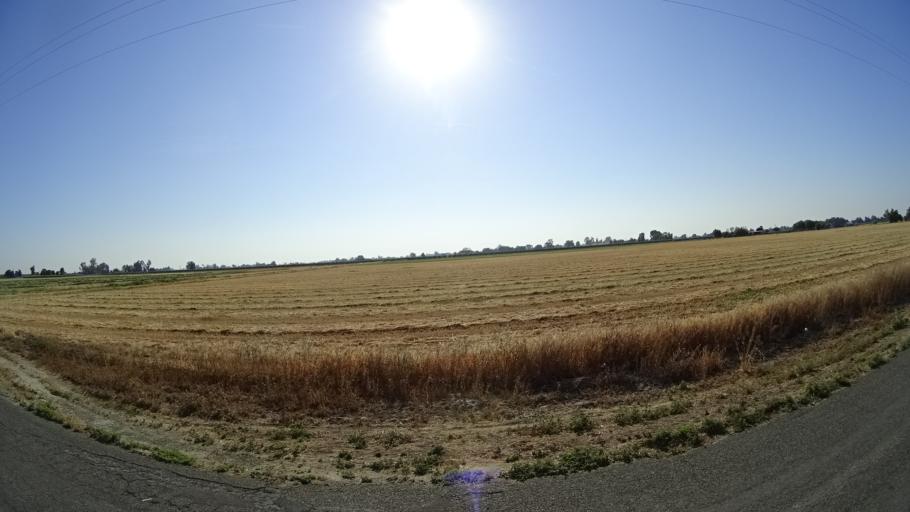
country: US
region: California
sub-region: Fresno County
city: Riverdale
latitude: 36.3618
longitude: -119.8693
